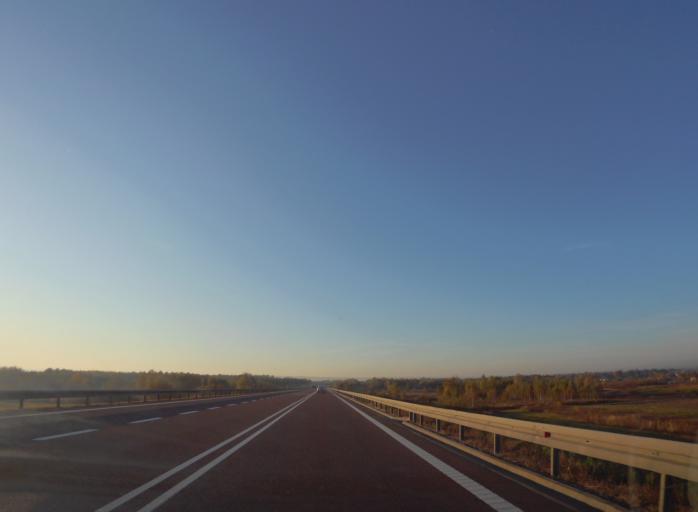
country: PL
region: Subcarpathian Voivodeship
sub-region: Powiat rzeszowski
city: Wolka Podlesna
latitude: 50.1361
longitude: 22.0795
